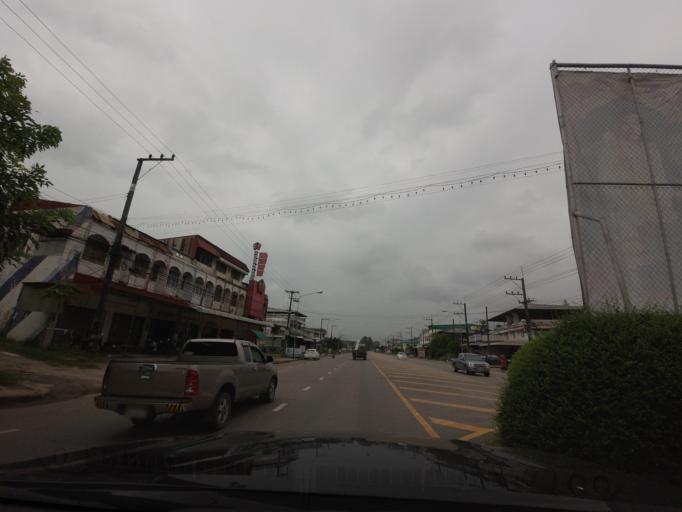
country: TH
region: Nong Khai
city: Si Chiang Mai
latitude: 17.9566
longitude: 102.5822
